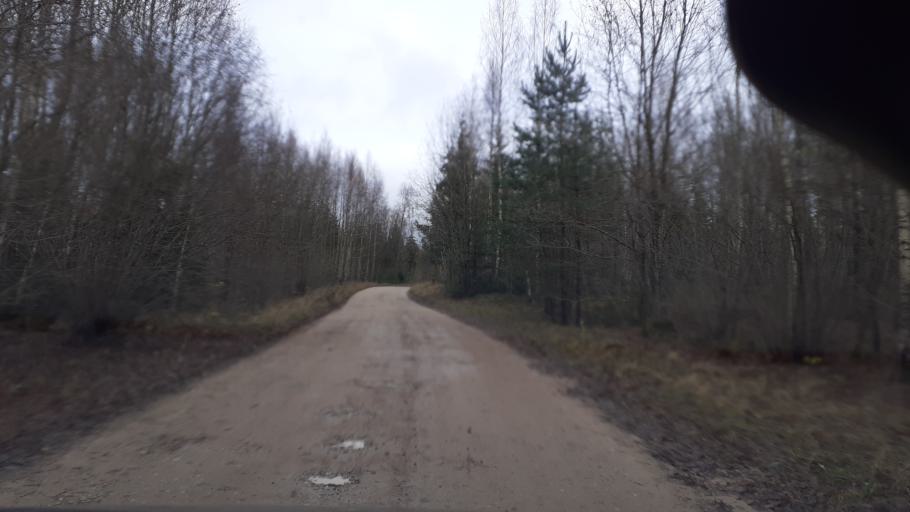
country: LV
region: Kuldigas Rajons
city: Kuldiga
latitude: 57.0298
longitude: 21.8708
